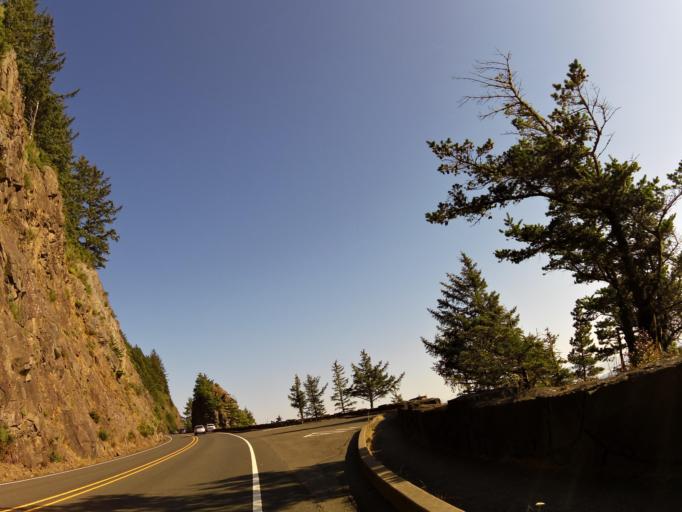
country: US
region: Oregon
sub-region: Tillamook County
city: Rockaway Beach
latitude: 45.7442
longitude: -123.9595
